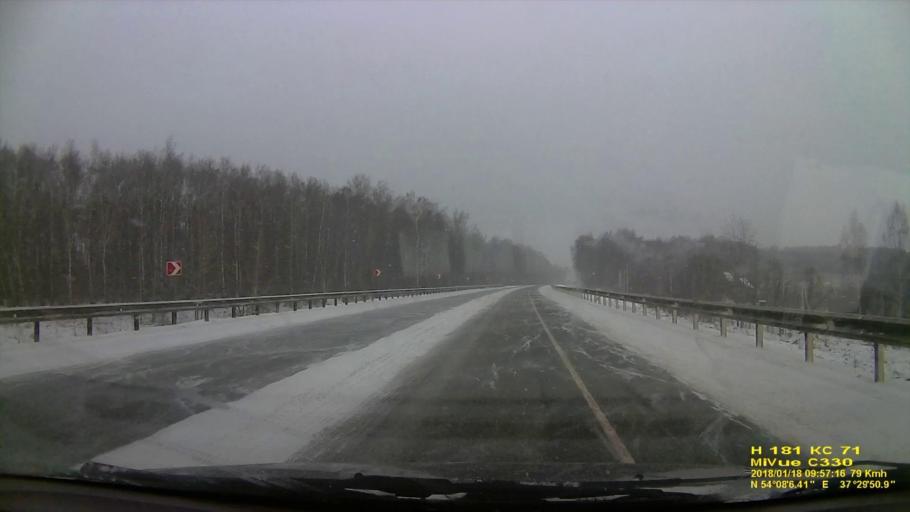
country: RU
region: Tula
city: Kosaya Gora
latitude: 54.1350
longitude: 37.4974
